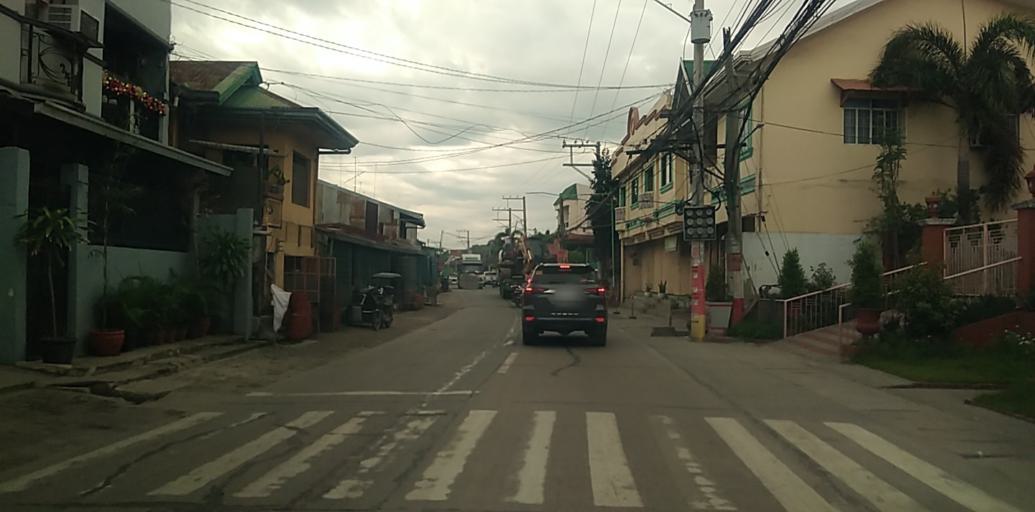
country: PH
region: Central Luzon
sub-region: Province of Pampanga
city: San Fernando
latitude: 15.0043
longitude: 120.7062
